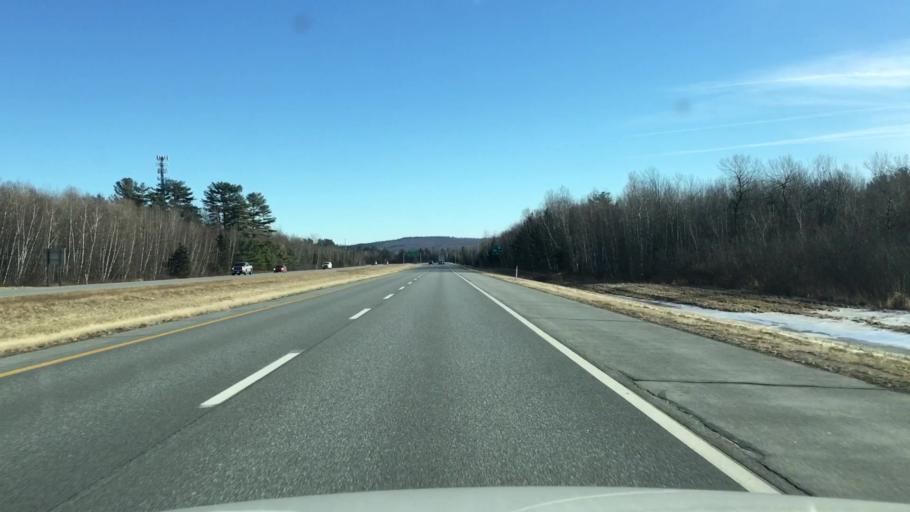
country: US
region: Maine
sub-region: Penobscot County
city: Brewer
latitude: 44.7720
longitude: -68.7426
